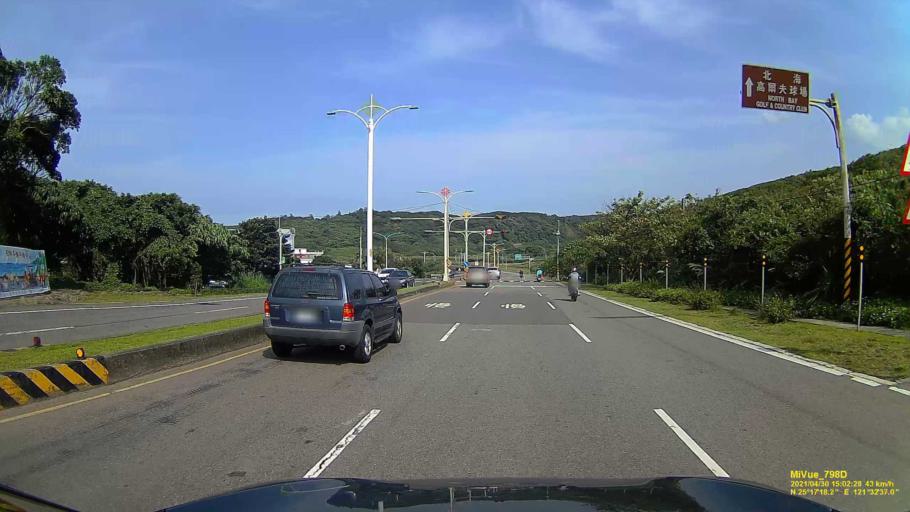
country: TW
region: Taipei
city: Taipei
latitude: 25.2883
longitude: 121.5438
